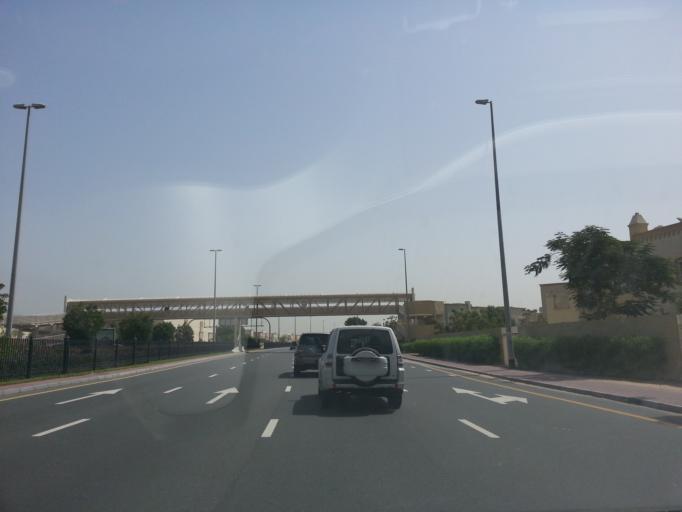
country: AE
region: Dubai
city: Dubai
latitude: 25.0526
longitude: 55.1713
